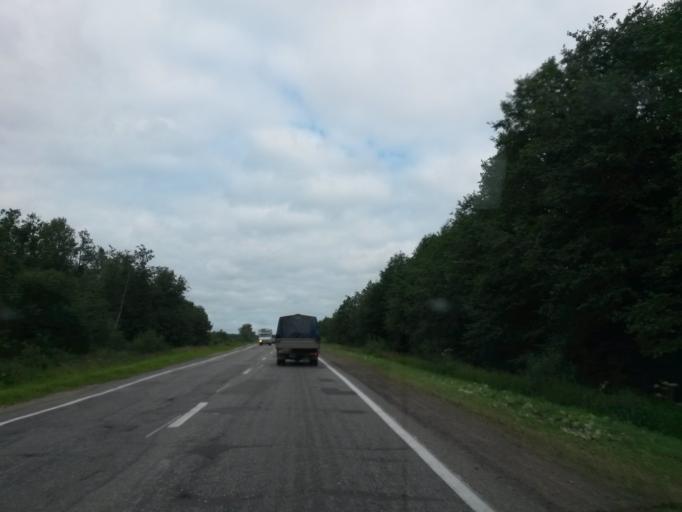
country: RU
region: Jaroslavl
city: Gavrilov-Yam
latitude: 57.4397
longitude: 39.9173
